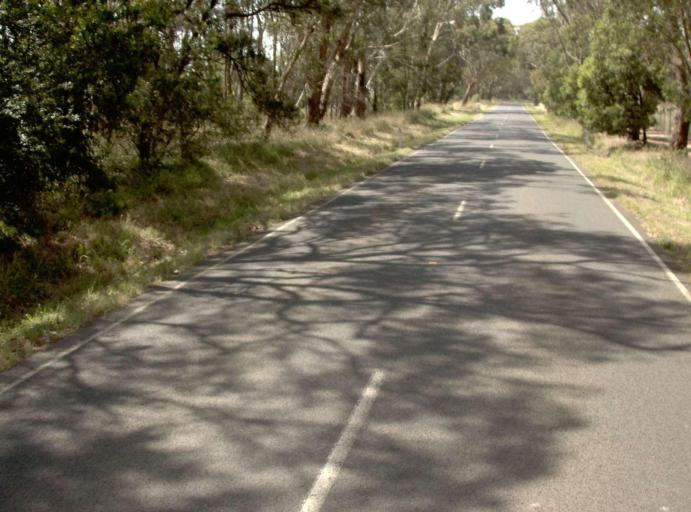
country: AU
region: Victoria
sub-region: Latrobe
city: Traralgon
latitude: -38.2630
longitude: 146.5464
